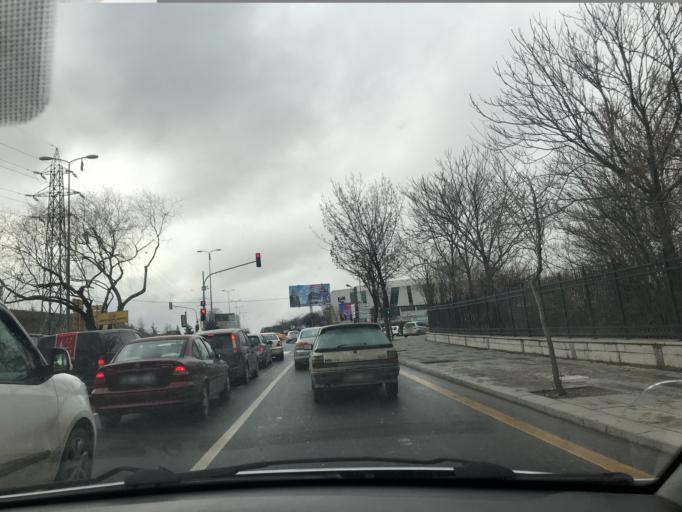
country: TR
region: Ankara
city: Batikent
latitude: 39.9598
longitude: 32.7822
